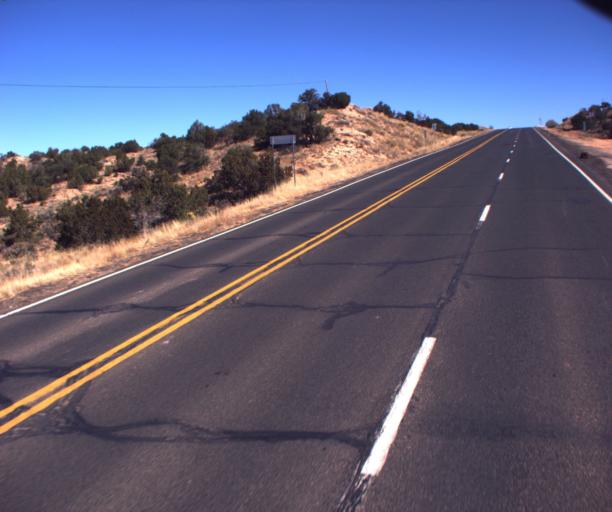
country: US
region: Arizona
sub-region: Apache County
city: Ganado
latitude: 35.7101
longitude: -109.5228
